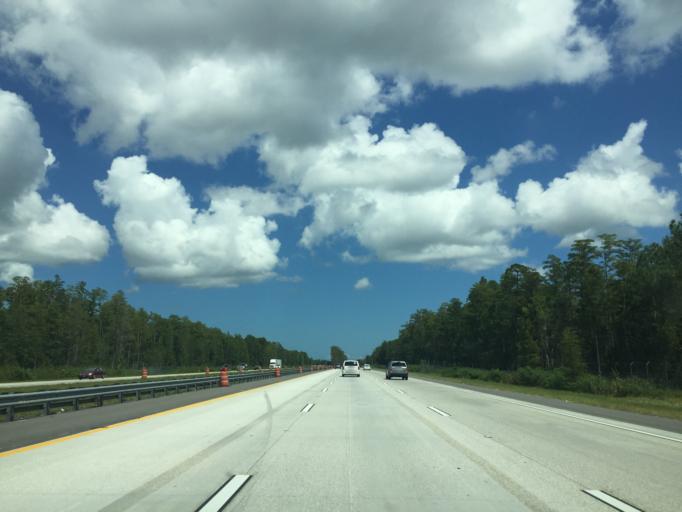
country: US
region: Florida
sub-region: Volusia County
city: Samsula-Spruce Creek
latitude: 29.0853
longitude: -81.1675
